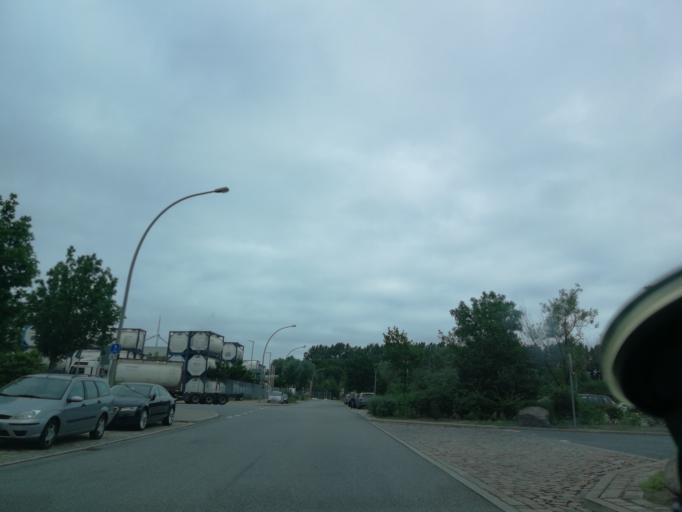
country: DE
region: Hamburg
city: Altona
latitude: 53.5080
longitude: 9.9257
